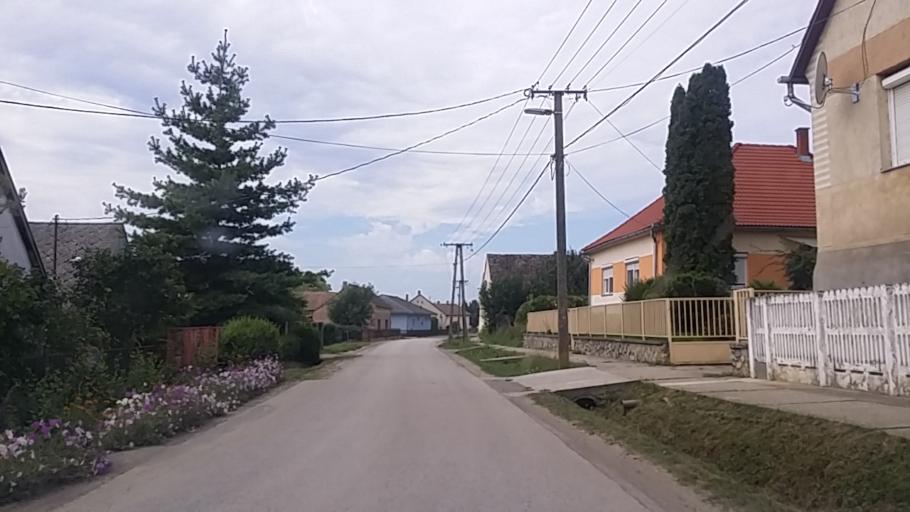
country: HU
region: Somogy
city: Taszar
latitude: 46.3507
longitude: 17.9905
